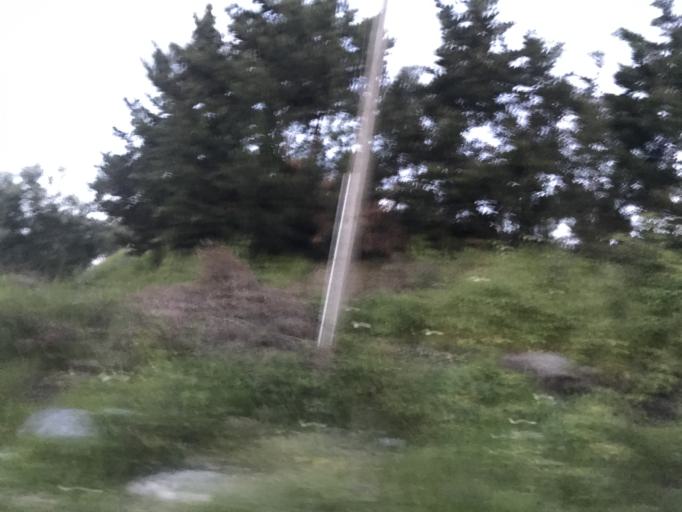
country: TR
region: Hatay
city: Uzunbag
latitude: 36.1200
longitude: 36.0448
